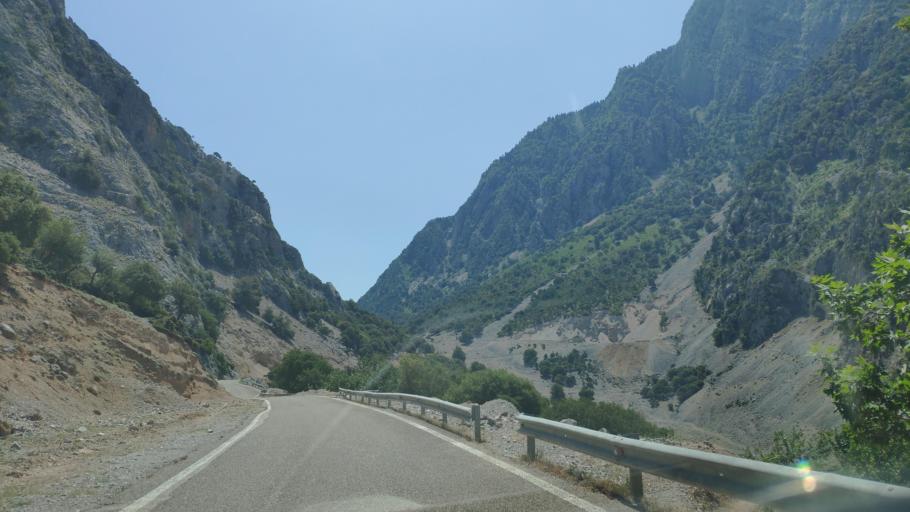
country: GR
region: West Greece
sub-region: Nomos Aitolias kai Akarnanias
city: Krikellos
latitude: 39.0246
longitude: 21.3318
